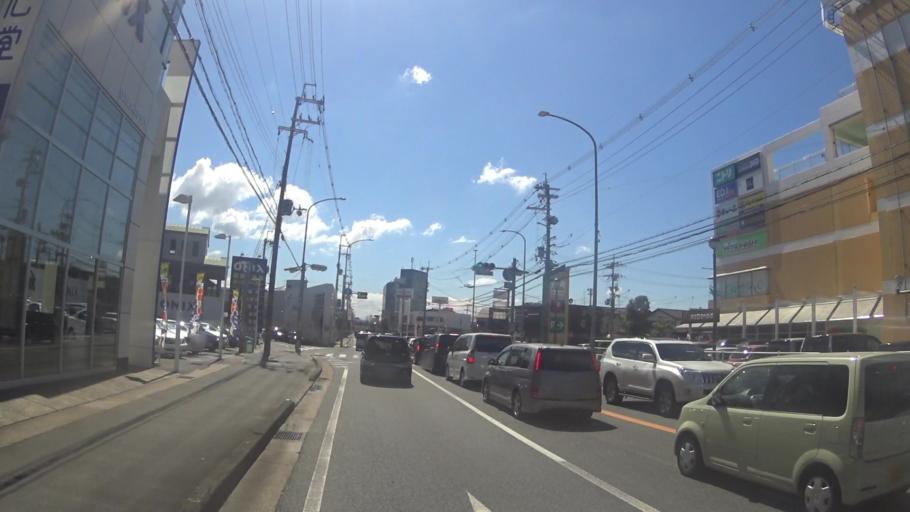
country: JP
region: Kyoto
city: Tanabe
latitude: 34.8430
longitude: 135.7872
